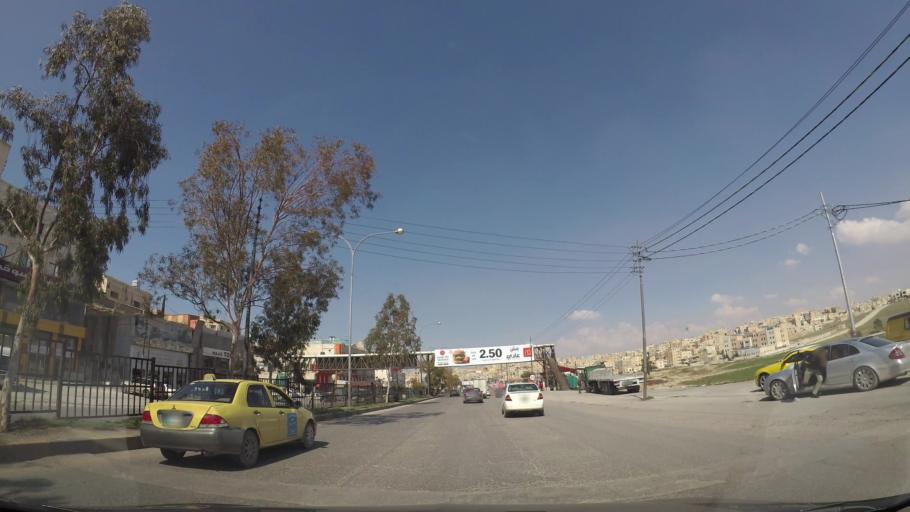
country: JO
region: Zarqa
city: Zarqa
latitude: 32.0356
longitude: 36.0915
